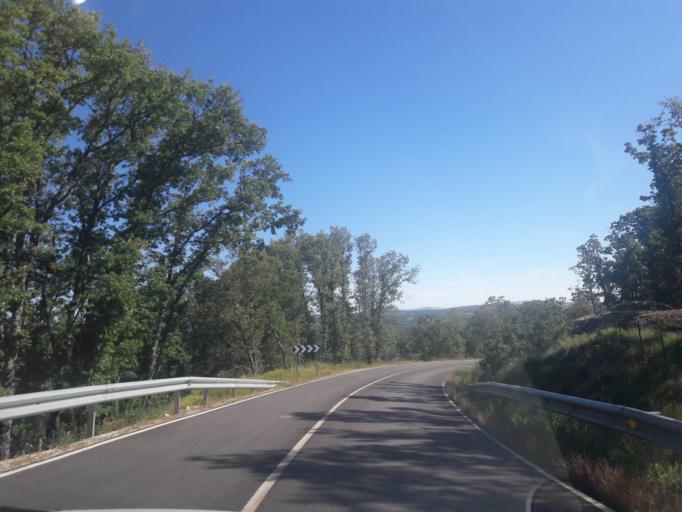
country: ES
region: Castille and Leon
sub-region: Provincia de Salamanca
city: Montemayor del Rio
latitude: 40.3401
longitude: -5.8856
